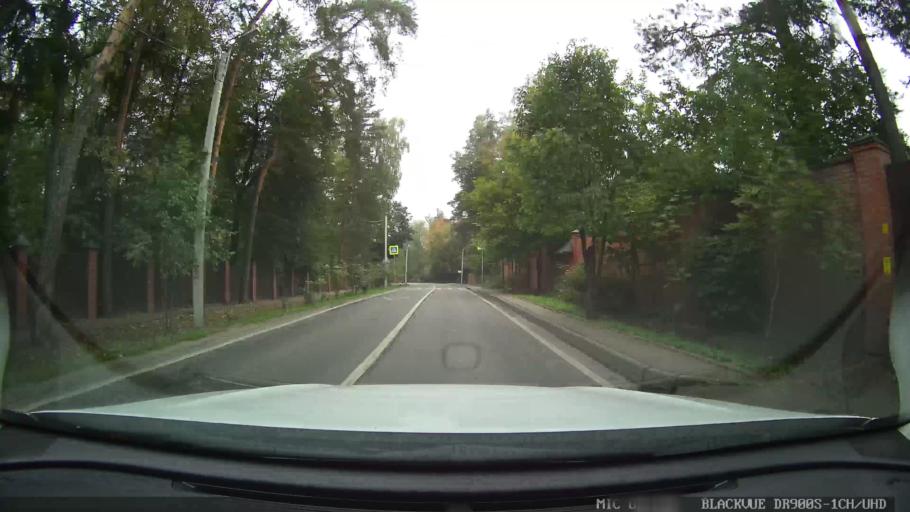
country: RU
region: Moscow
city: Novo-Peredelkino
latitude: 55.6520
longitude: 37.3555
